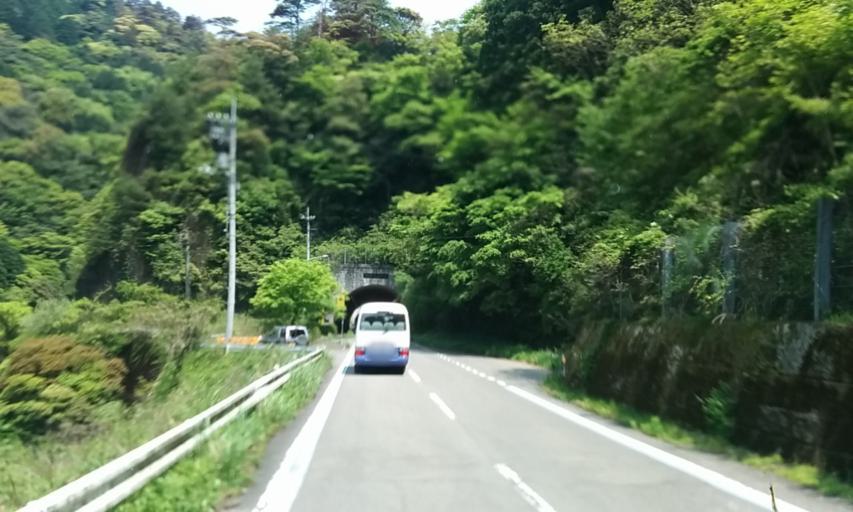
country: JP
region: Ehime
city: Niihama
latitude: 33.8843
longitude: 133.3037
